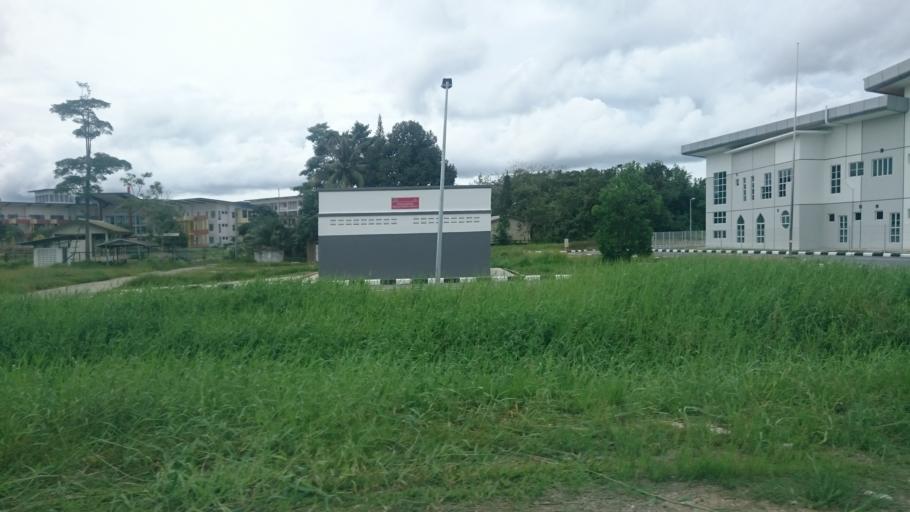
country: BN
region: Brunei and Muara
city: Bandar Seri Begawan
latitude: 4.8656
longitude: 114.8468
